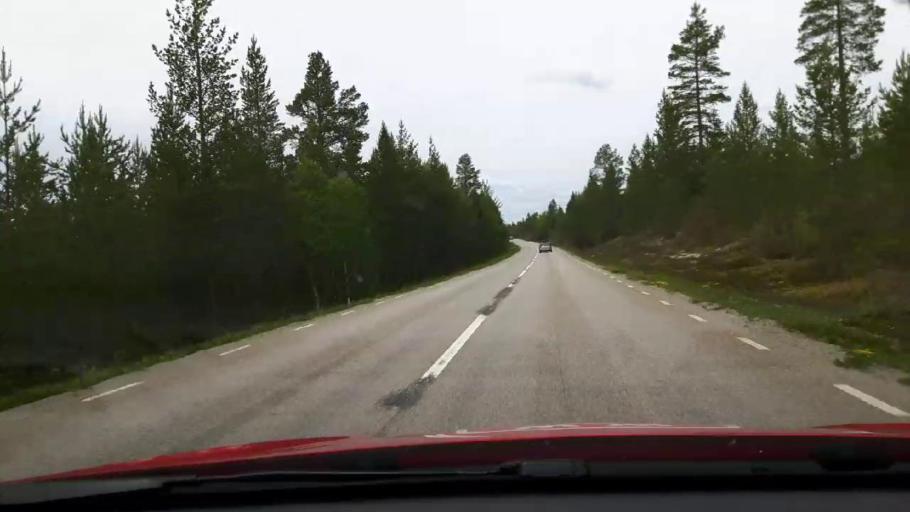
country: SE
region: Jaemtland
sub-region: Harjedalens Kommun
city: Sveg
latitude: 62.2355
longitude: 13.8532
